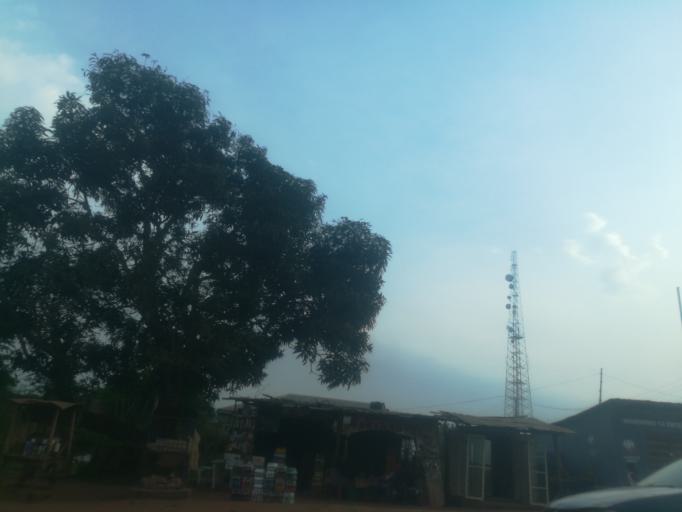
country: NG
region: Ogun
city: Abeokuta
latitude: 7.1405
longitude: 3.2657
